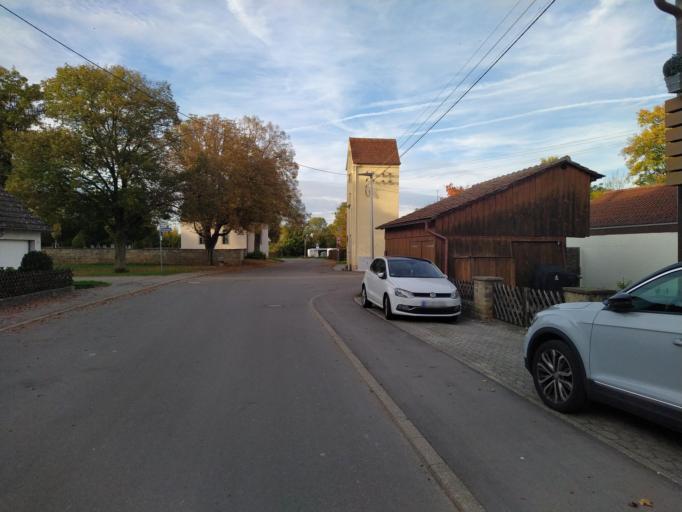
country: DE
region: Baden-Wuerttemberg
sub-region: Tuebingen Region
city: Rottenburg
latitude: 48.4777
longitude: 8.9726
